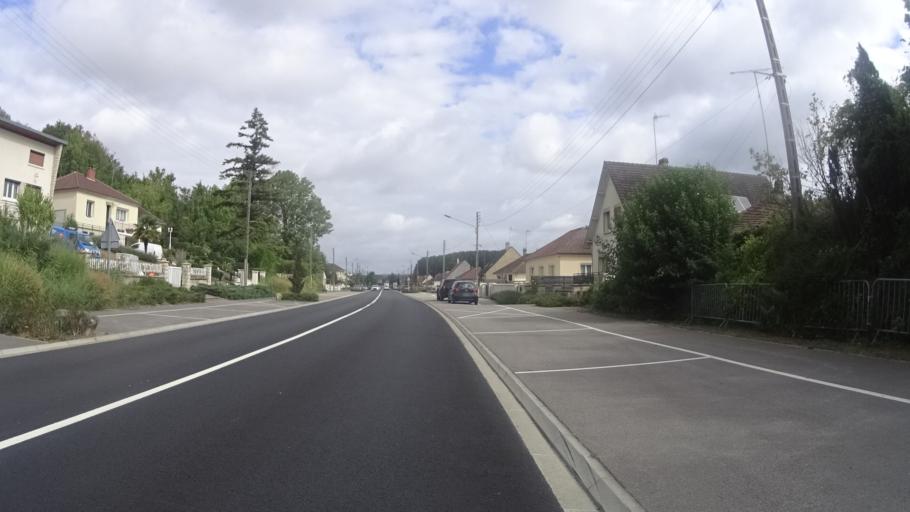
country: FR
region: Picardie
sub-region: Departement de l'Oise
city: Choisy-au-Bac
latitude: 49.4451
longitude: 2.8638
